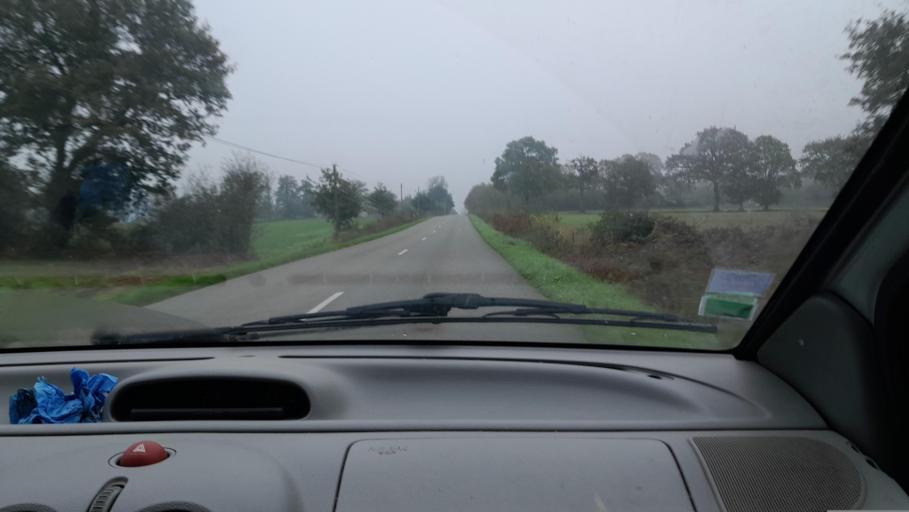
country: FR
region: Brittany
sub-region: Departement d'Ille-et-Vilaine
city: Le Pertre
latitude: 47.9736
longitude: -1.0266
